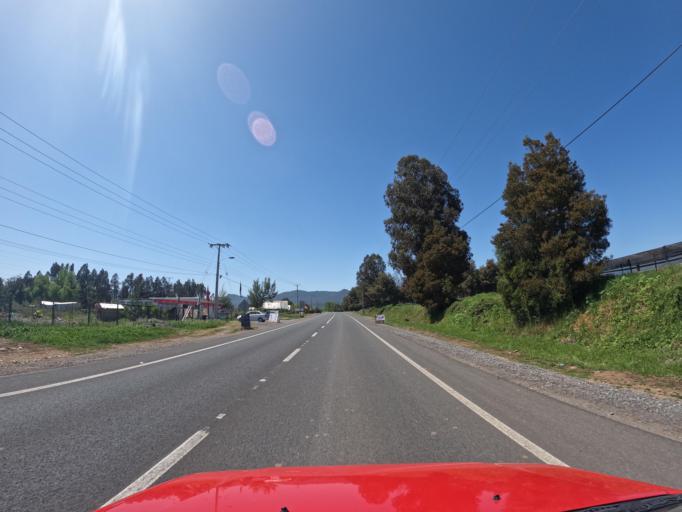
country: CL
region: Maule
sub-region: Provincia de Linares
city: Colbun
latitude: -35.7149
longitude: -71.4036
